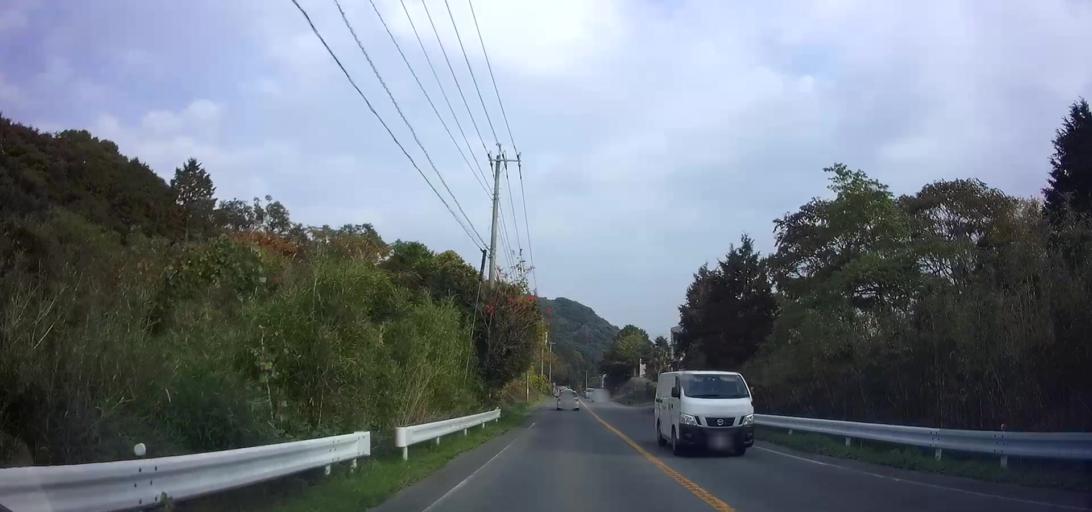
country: JP
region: Nagasaki
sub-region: Isahaya-shi
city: Isahaya
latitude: 32.7961
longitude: 130.1235
